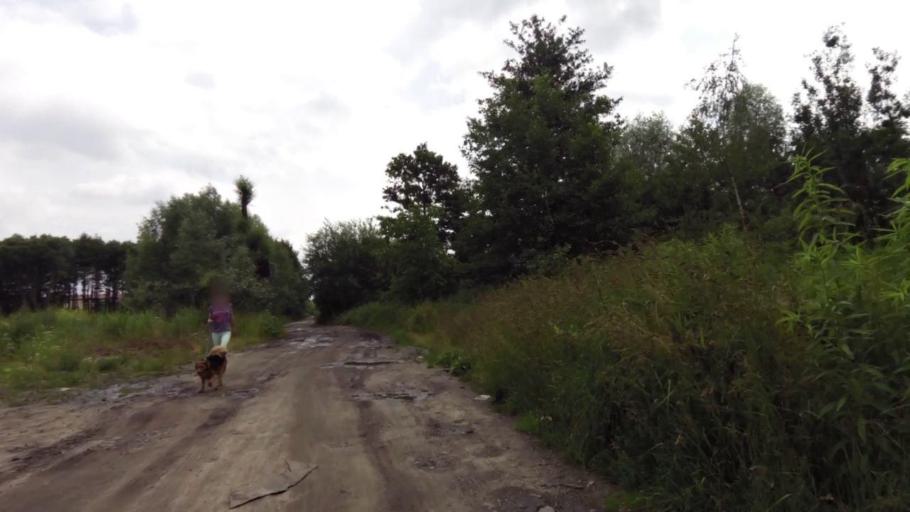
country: PL
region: West Pomeranian Voivodeship
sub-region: Szczecin
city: Szczecin
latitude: 53.4042
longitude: 14.6716
